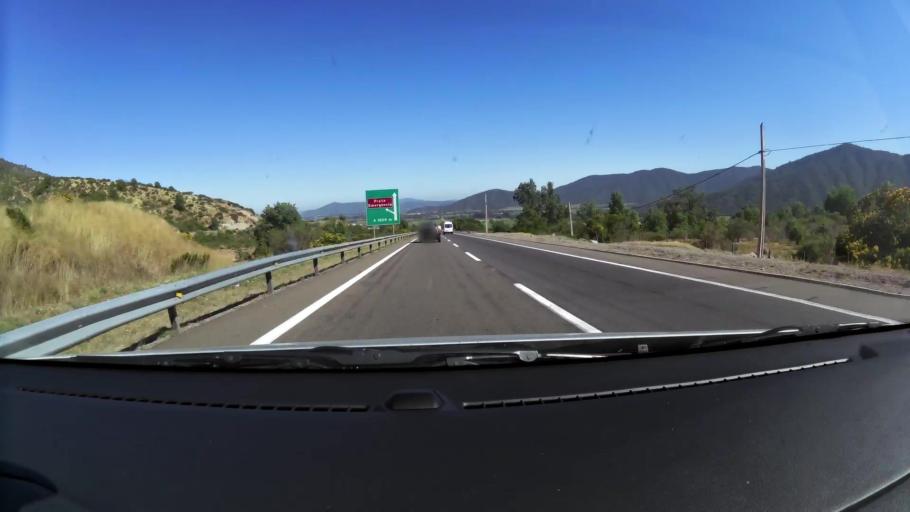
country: CL
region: Santiago Metropolitan
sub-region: Provincia de Melipilla
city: Melipilla
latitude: -33.3830
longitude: -71.2752
